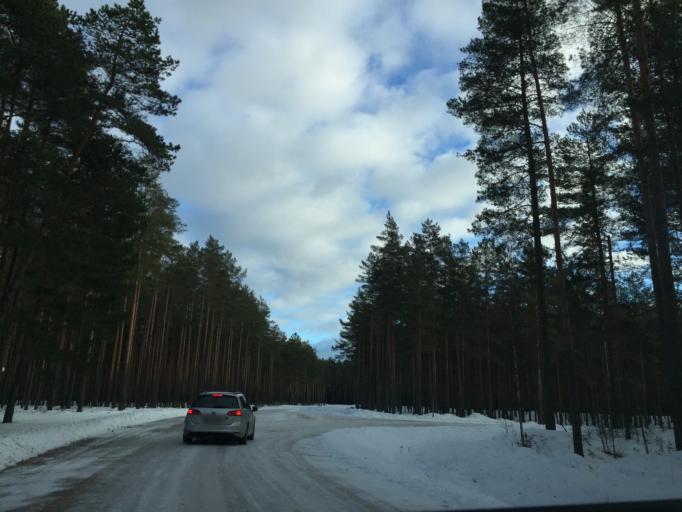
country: LV
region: Ogre
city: Jumprava
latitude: 56.5606
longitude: 24.8539
